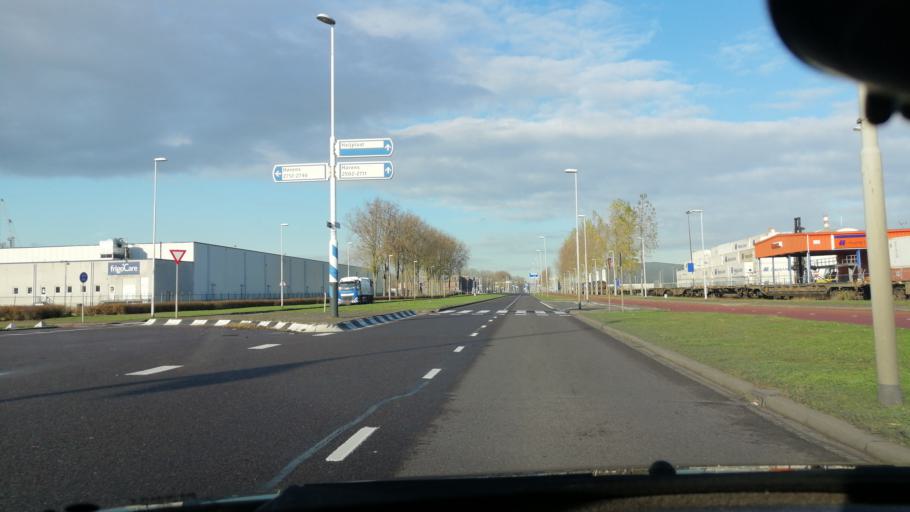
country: NL
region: South Holland
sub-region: Gemeente Albrandswaard
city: Rhoon
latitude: 51.8805
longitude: 4.4313
